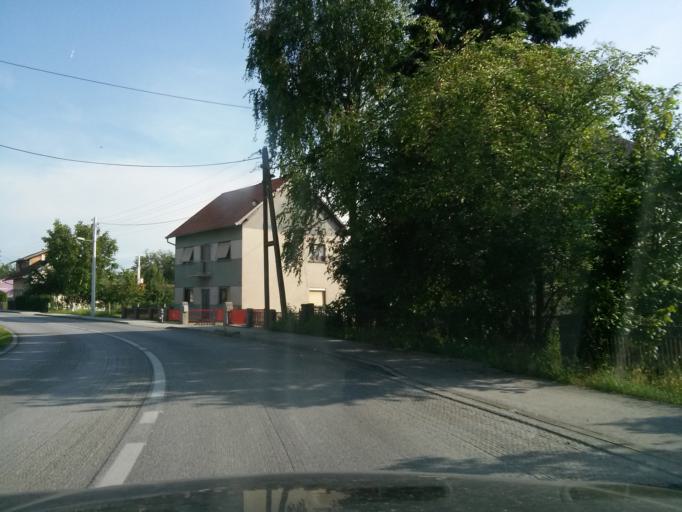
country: HR
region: Grad Zagreb
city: Strmec
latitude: 45.7056
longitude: 15.8925
